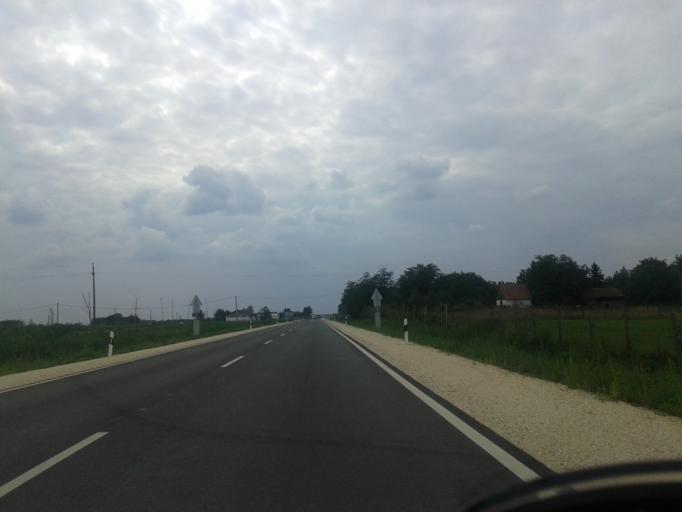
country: HU
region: Bacs-Kiskun
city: Kisszallas
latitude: 46.2724
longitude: 19.5415
